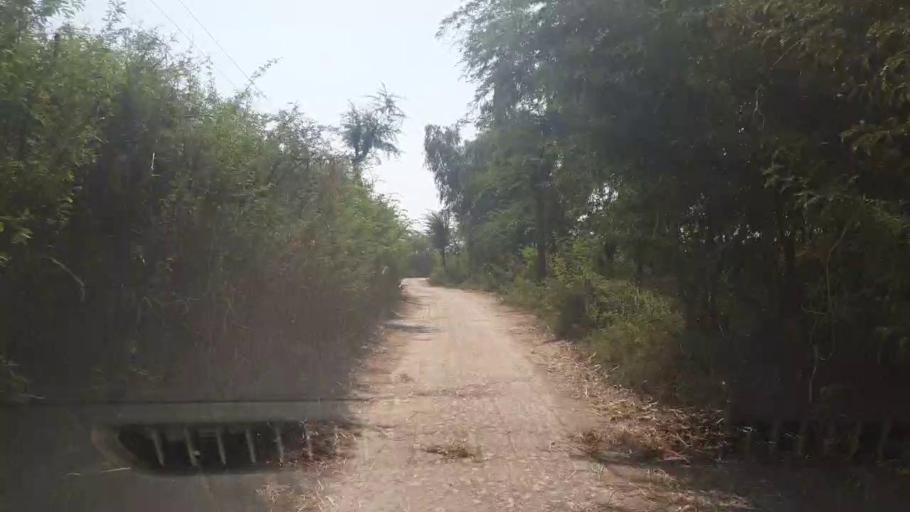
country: PK
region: Sindh
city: Badin
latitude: 24.6309
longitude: 68.9128
